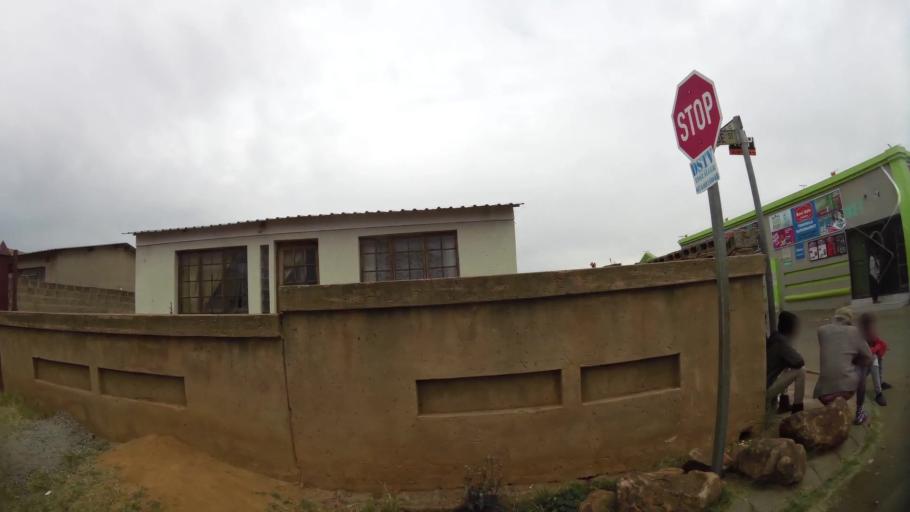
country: ZA
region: Gauteng
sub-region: City of Tshwane Metropolitan Municipality
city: Cullinan
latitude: -25.7069
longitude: 28.3588
